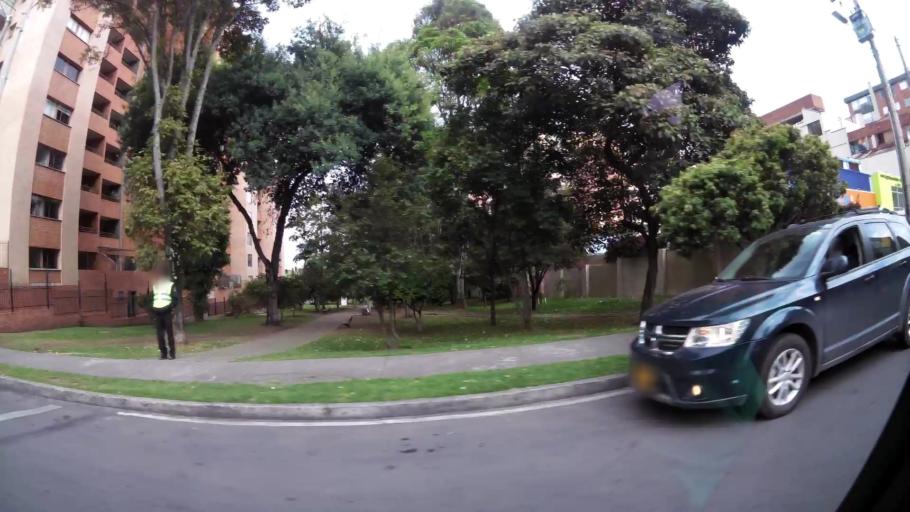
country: CO
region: Bogota D.C.
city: Barrio San Luis
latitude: 4.7155
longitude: -74.0308
